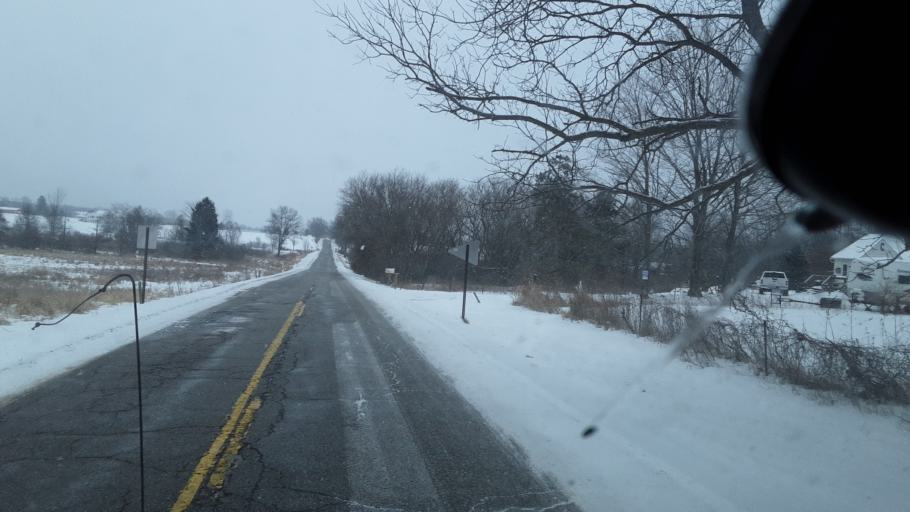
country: US
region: Michigan
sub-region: Ingham County
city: Leslie
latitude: 42.4896
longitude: -84.3408
